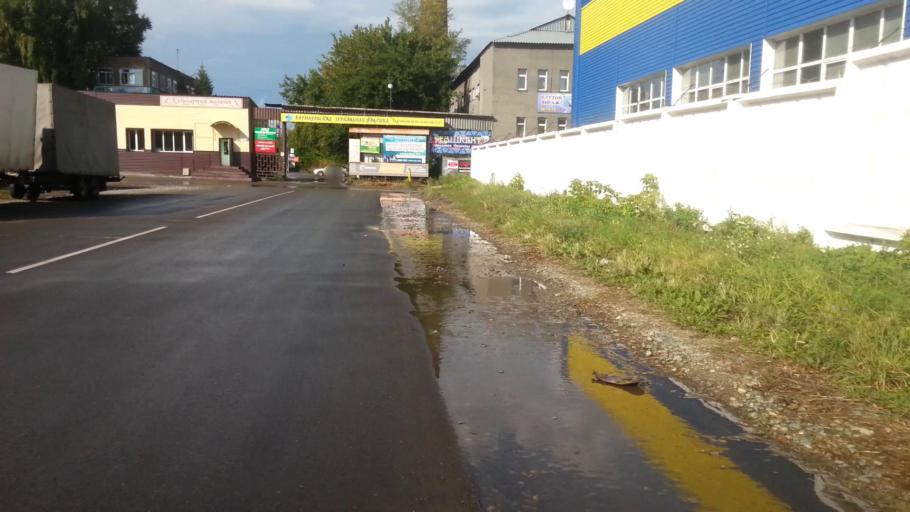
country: RU
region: Altai Krai
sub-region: Gorod Barnaulskiy
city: Barnaul
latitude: 53.3440
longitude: 83.7231
